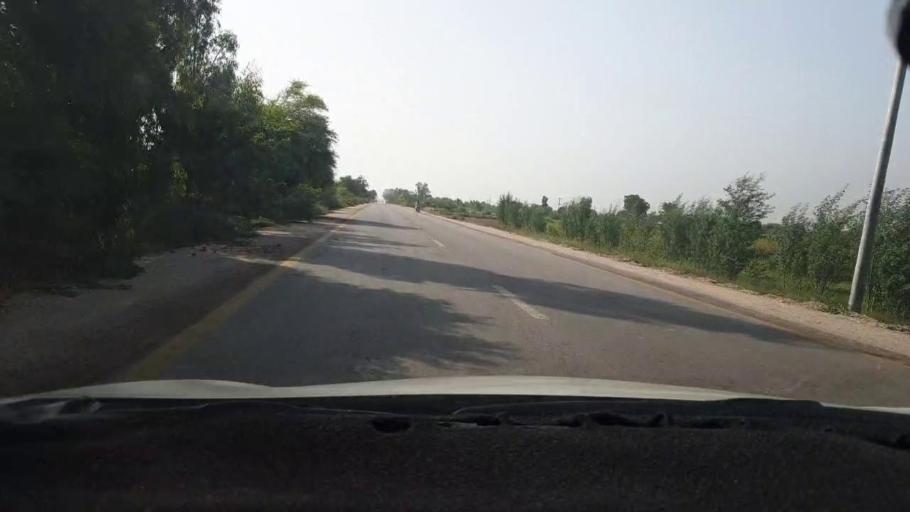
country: PK
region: Sindh
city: Sanghar
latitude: 26.0011
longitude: 68.9622
